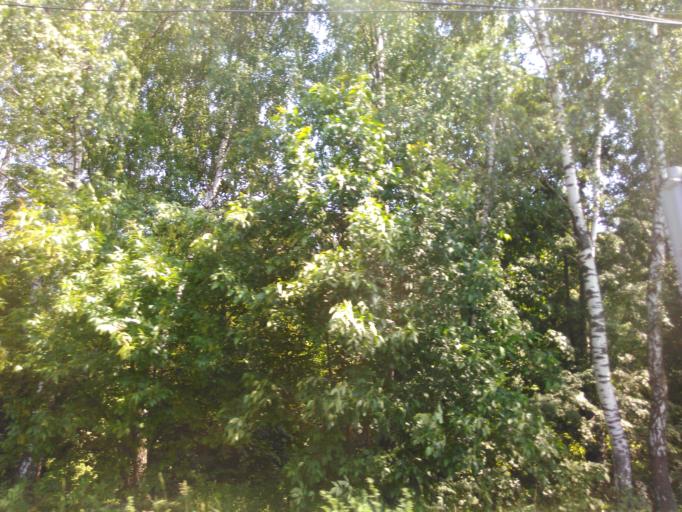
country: RU
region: Moskovskaya
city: Staraya Kupavna
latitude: 55.8142
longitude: 38.1627
